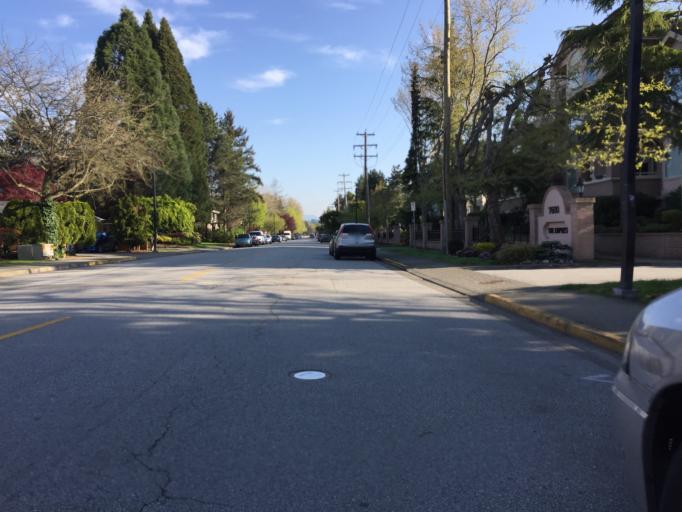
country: CA
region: British Columbia
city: Richmond
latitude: 49.1569
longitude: -123.1436
